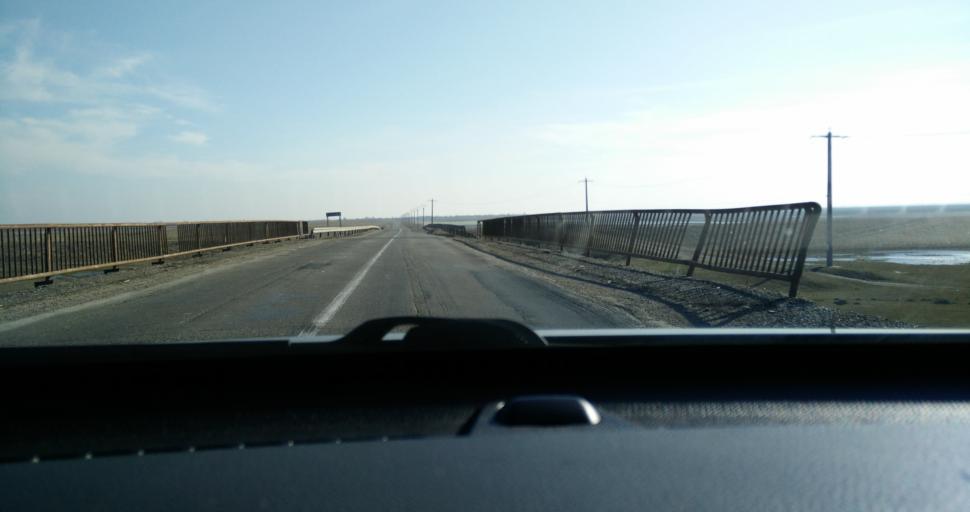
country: RO
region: Vrancea
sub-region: Comuna Nanesti
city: Nanesti
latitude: 45.5755
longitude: 27.4979
